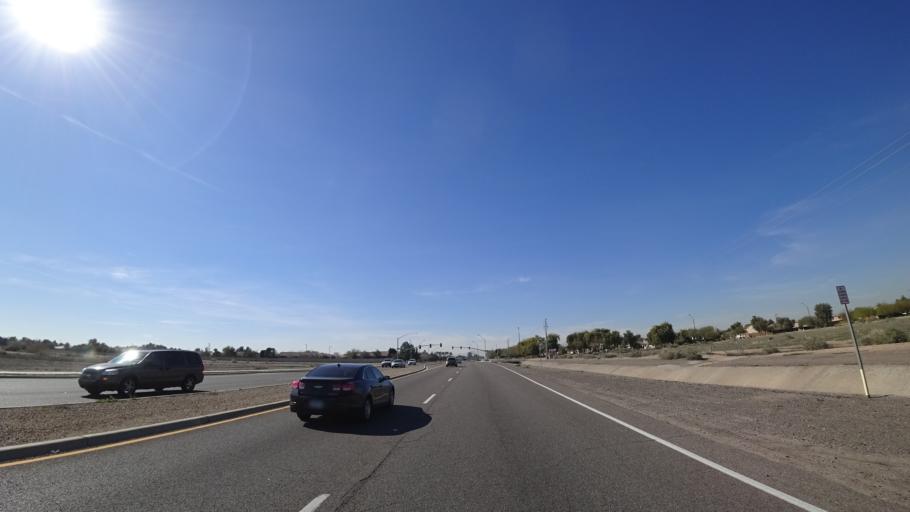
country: US
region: Arizona
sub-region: Maricopa County
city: Litchfield Park
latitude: 33.5076
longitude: -112.3263
